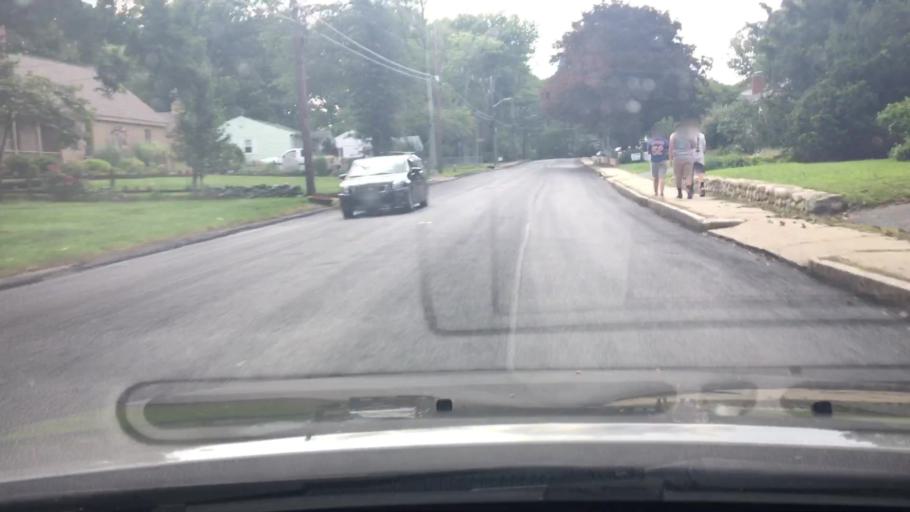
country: US
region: Massachusetts
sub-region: Worcester County
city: Milford
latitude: 42.1579
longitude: -71.5360
